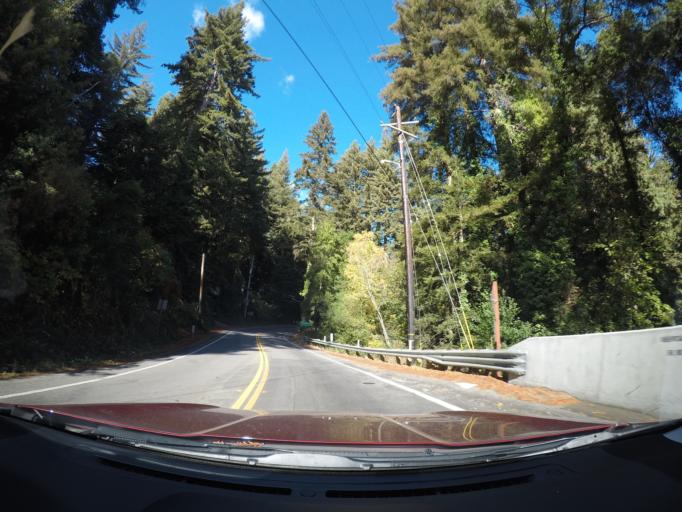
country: US
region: California
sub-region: Santa Cruz County
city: Brookdale
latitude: 37.1045
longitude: -122.1047
